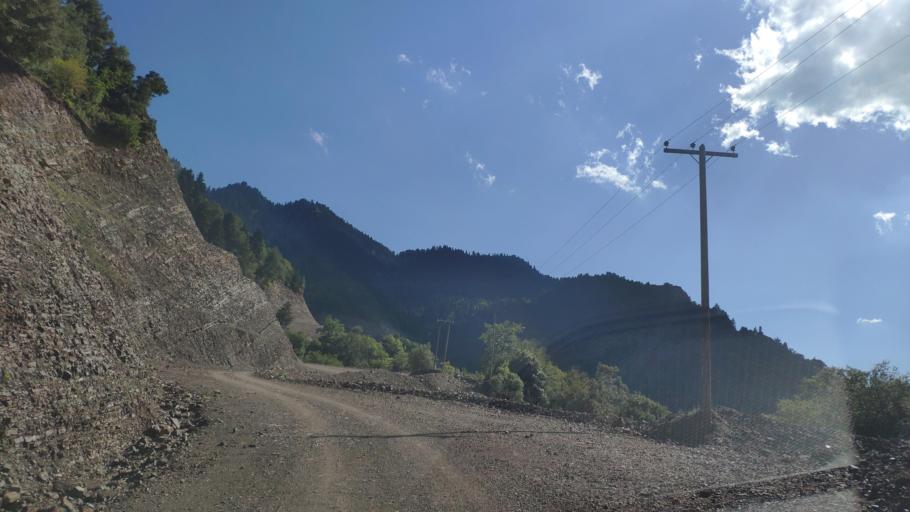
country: GR
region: Central Greece
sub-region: Nomos Evrytanias
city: Kerasochori
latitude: 39.1227
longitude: 21.6257
